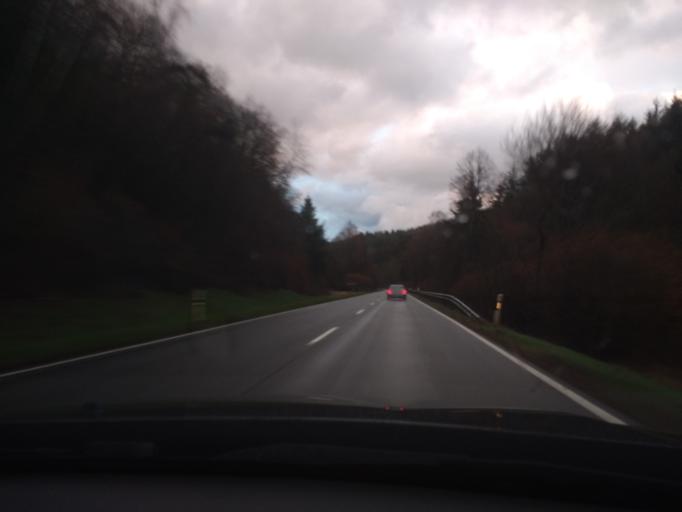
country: DE
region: Rheinland-Pfalz
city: Breit
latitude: 49.7668
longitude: 6.9005
